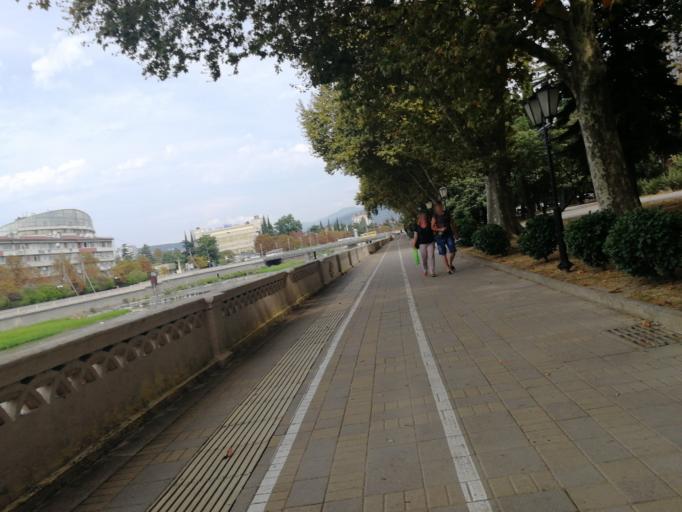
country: RU
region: Krasnodarskiy
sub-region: Sochi City
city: Sochi
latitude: 43.5925
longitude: 39.7202
